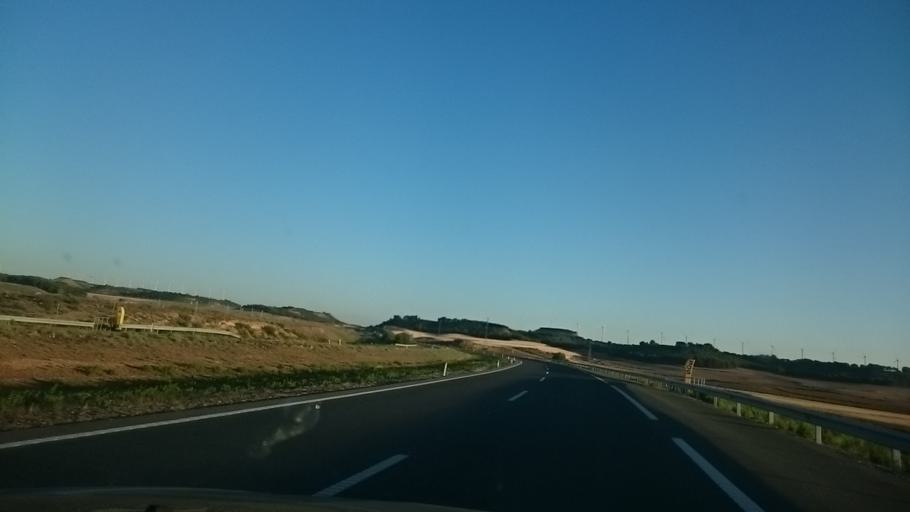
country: ES
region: Navarre
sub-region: Provincia de Navarra
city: Murchante
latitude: 42.0715
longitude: -1.6922
